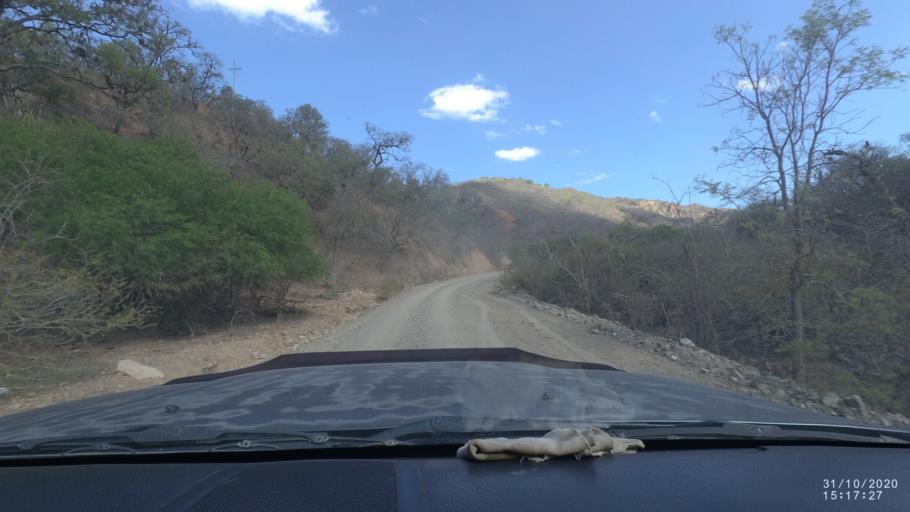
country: BO
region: Cochabamba
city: Aiquile
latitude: -18.3399
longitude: -64.7676
